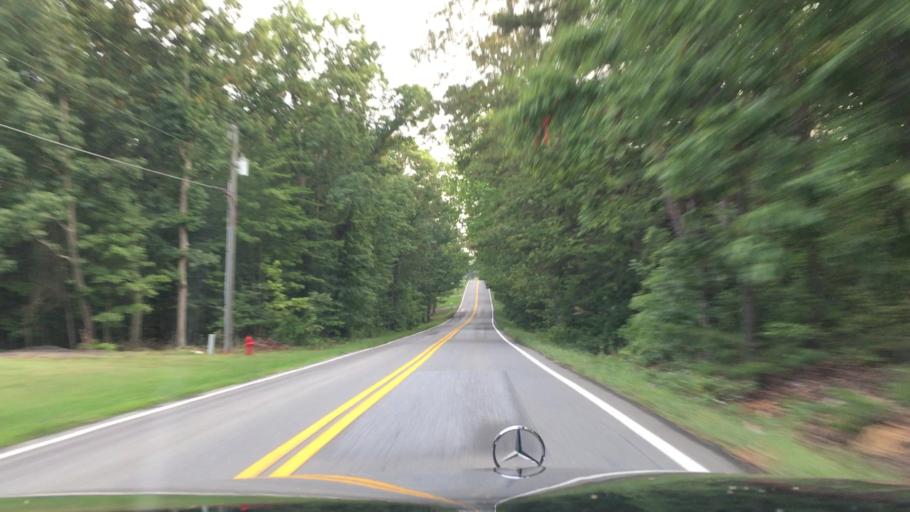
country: US
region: Virginia
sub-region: Campbell County
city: Timberlake
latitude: 37.2719
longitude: -79.2575
